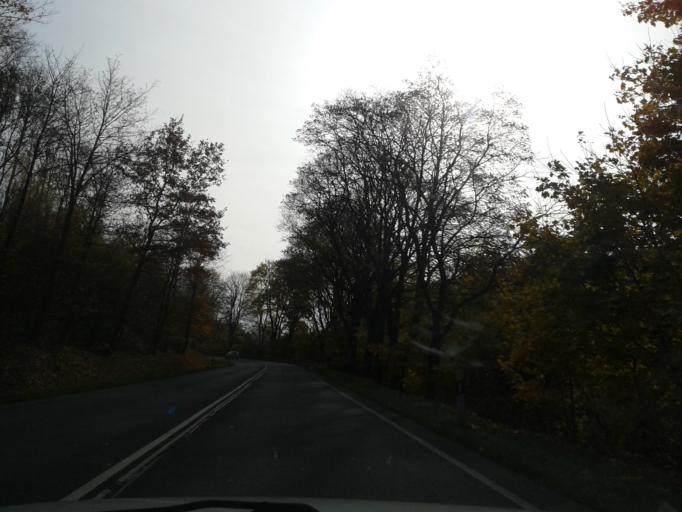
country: DE
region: North Rhine-Westphalia
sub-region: Regierungsbezirk Arnsberg
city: Olsberg
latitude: 51.3249
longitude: 8.4950
